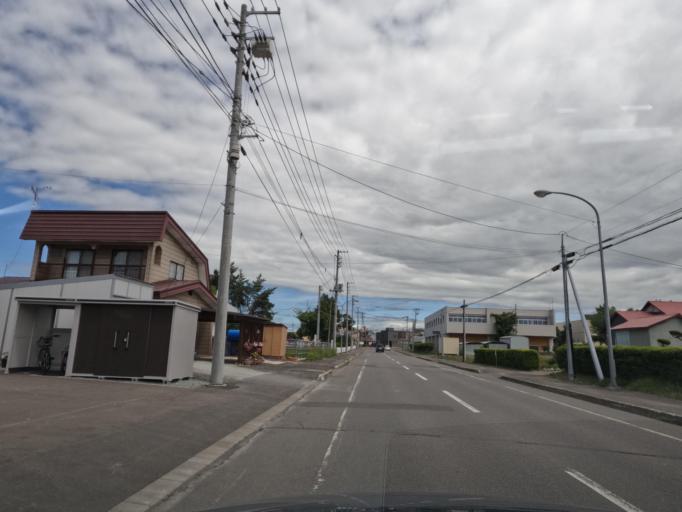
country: JP
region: Hokkaido
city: Shimo-furano
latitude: 43.4580
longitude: 142.4650
